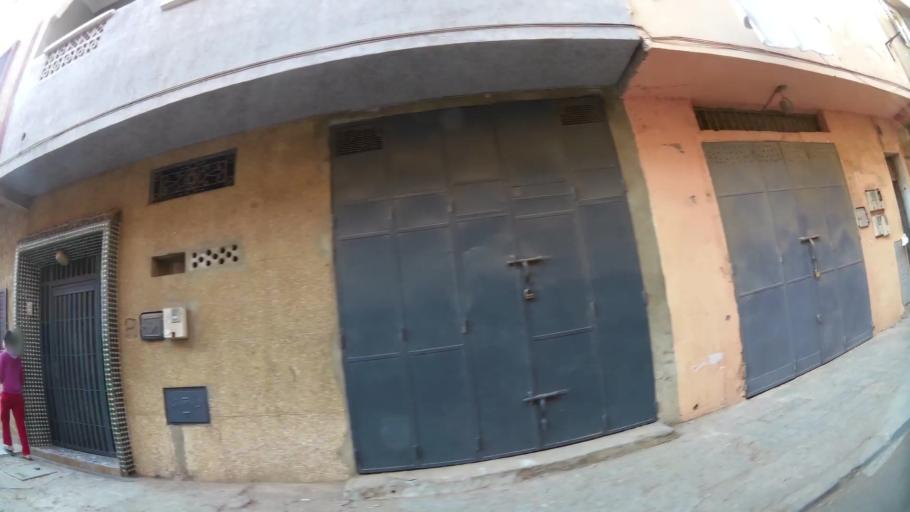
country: MA
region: Rabat-Sale-Zemmour-Zaer
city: Sale
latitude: 34.0544
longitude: -6.7897
